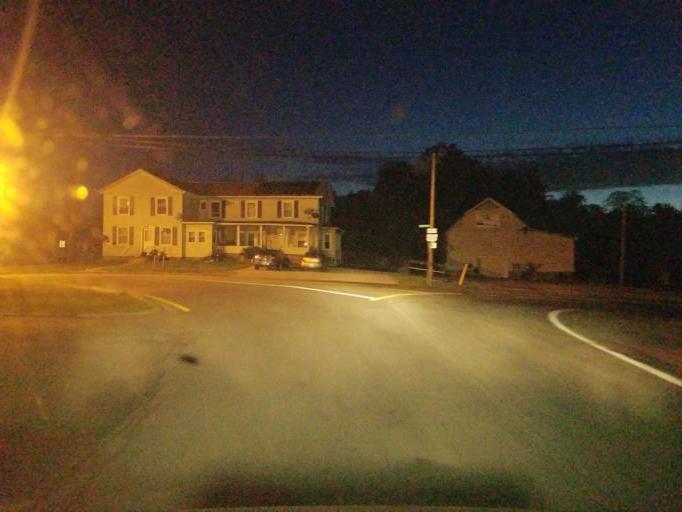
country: US
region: Ohio
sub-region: Lake County
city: Madison
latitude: 41.6899
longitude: -81.0508
